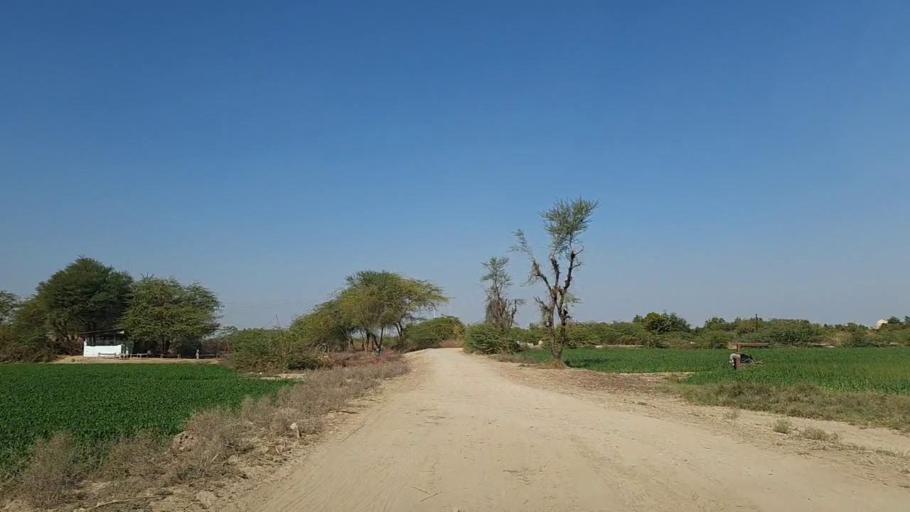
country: PK
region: Sindh
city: Nawabshah
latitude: 26.2548
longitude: 68.4412
